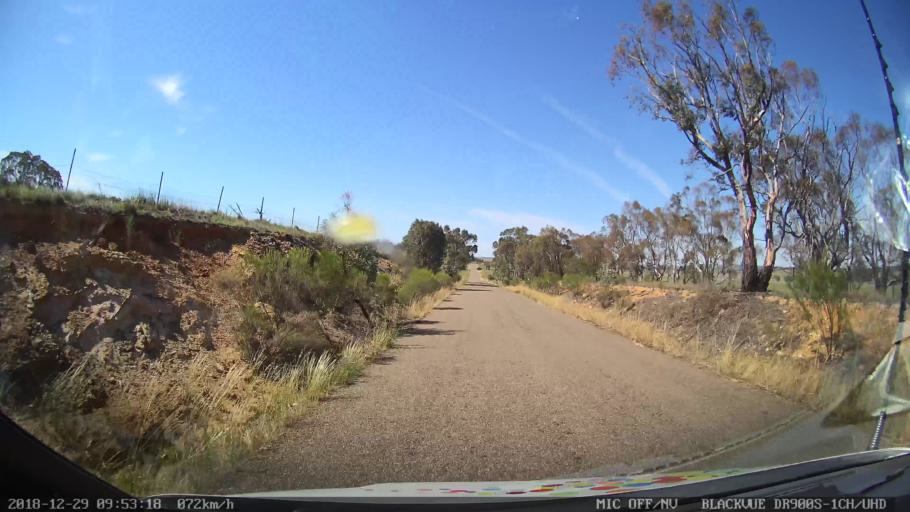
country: AU
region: New South Wales
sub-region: Goulburn Mulwaree
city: Goulburn
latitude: -34.7501
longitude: 149.4698
